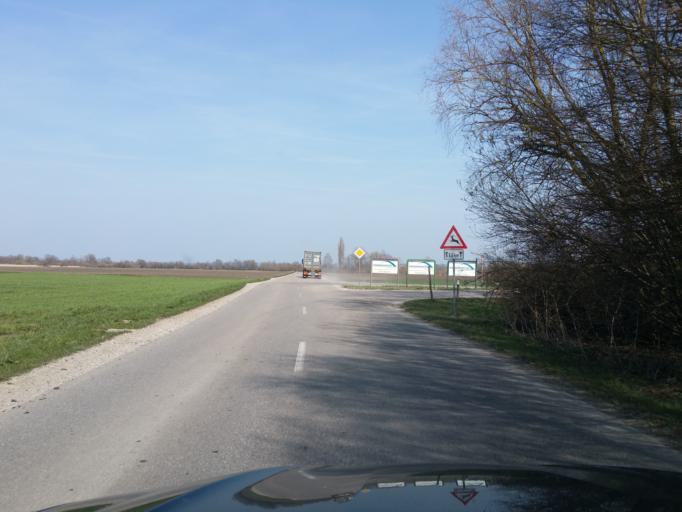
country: DE
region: Bavaria
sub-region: Upper Bavaria
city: Eitting
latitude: 48.3930
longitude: 11.8965
